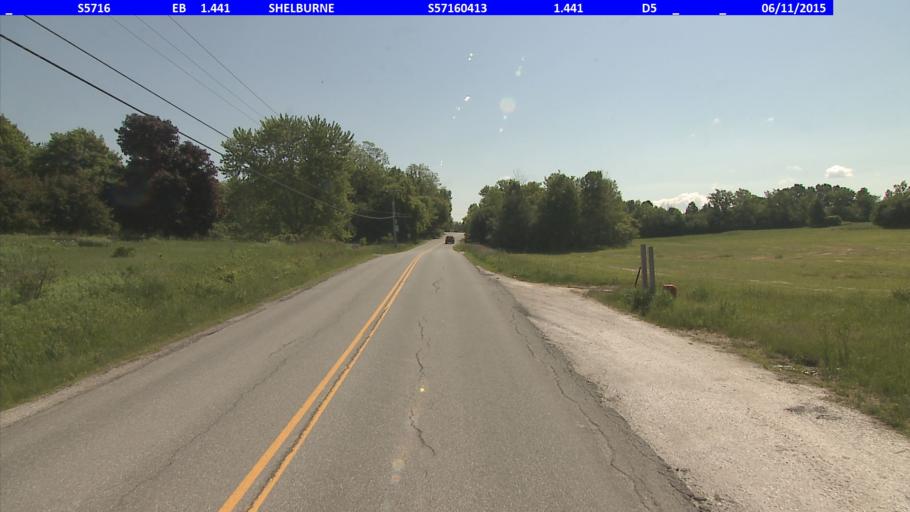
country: US
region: Vermont
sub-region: Chittenden County
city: Hinesburg
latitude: 44.3715
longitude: -73.1837
